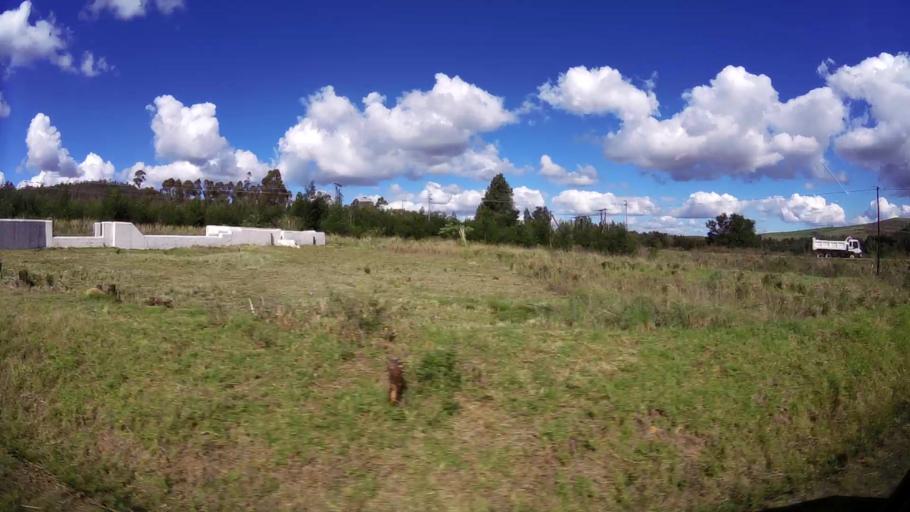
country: ZA
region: Western Cape
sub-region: Overberg District Municipality
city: Swellendam
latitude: -34.0255
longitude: 20.4205
